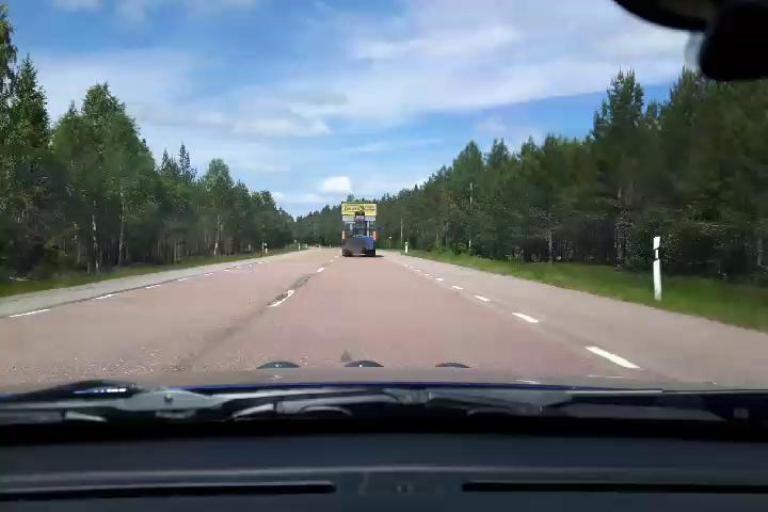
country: SE
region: Uppsala
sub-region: Osthammars Kommun
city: Bjorklinge
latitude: 60.1299
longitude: 17.5096
